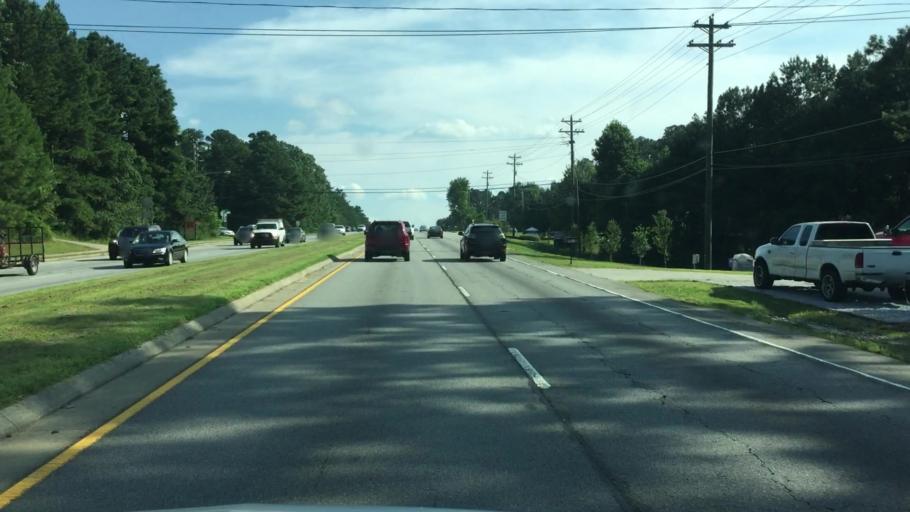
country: US
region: Georgia
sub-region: Gwinnett County
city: Snellville
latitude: 33.8960
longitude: -84.0069
